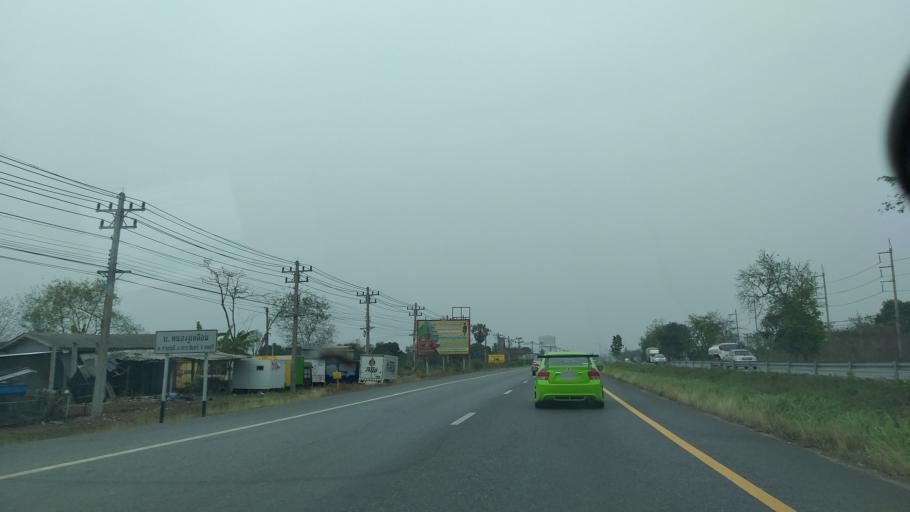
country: TH
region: Chon Buri
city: Ko Chan
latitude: 13.3507
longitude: 101.2711
